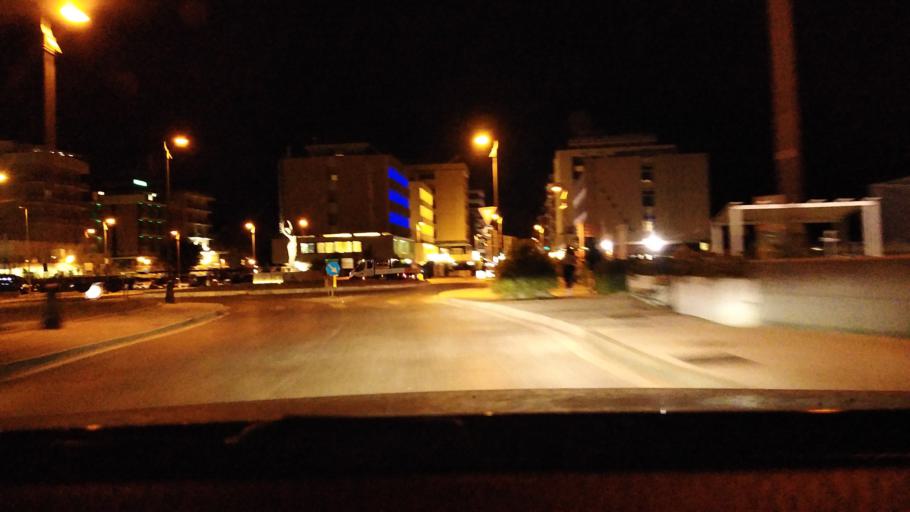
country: IT
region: Emilia-Romagna
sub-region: Provincia di Rimini
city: Bellaria-Igea Marina
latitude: 44.1288
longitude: 12.4882
